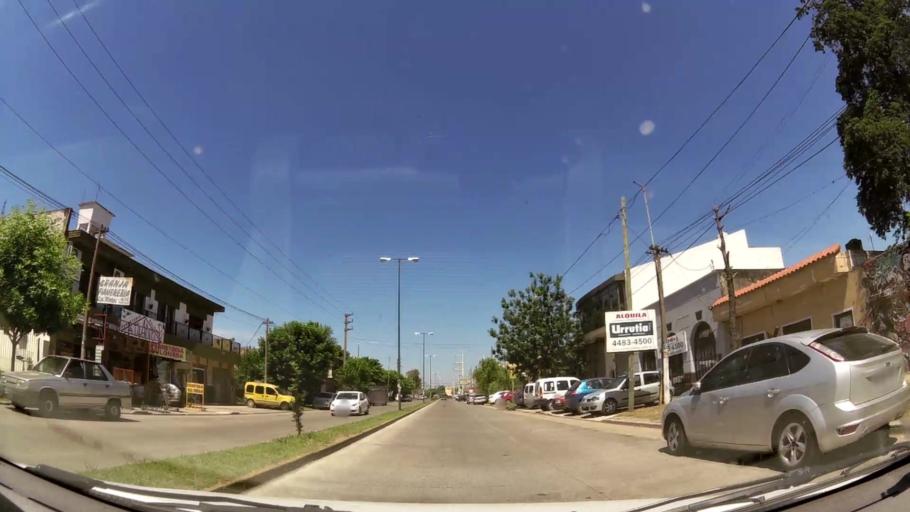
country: AR
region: Buenos Aires
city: Ituzaingo
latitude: -34.6785
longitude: -58.6694
